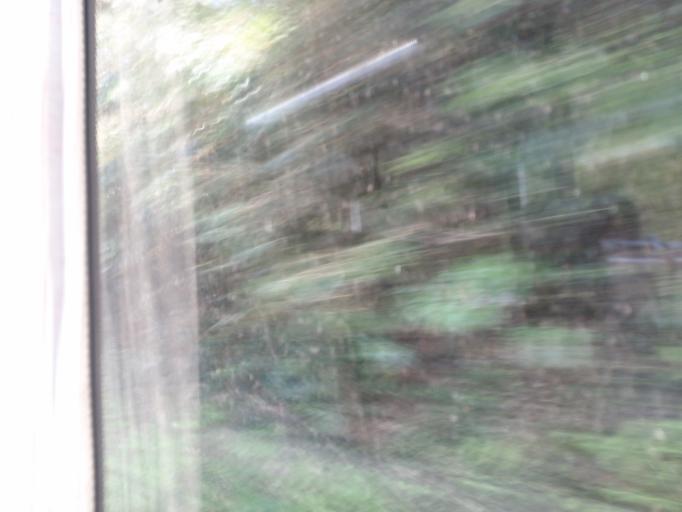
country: TW
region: Taipei
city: Taipei
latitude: 25.1753
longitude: 121.5414
